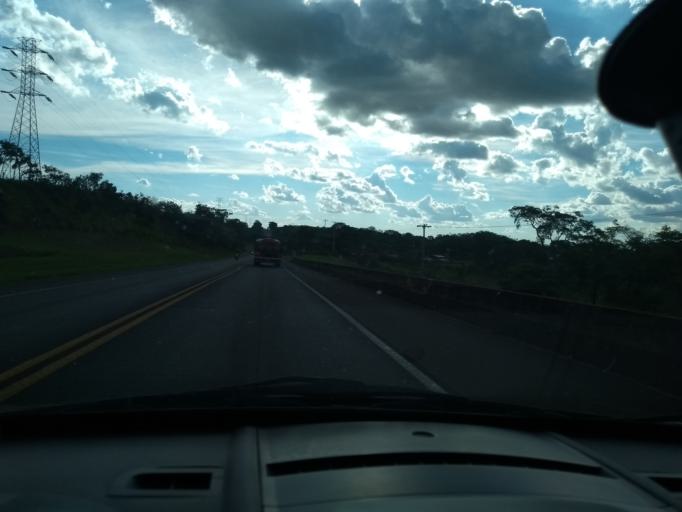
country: BR
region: Sao Paulo
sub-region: Casa Branca
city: Casa Branca
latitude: -21.7983
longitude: -47.0804
